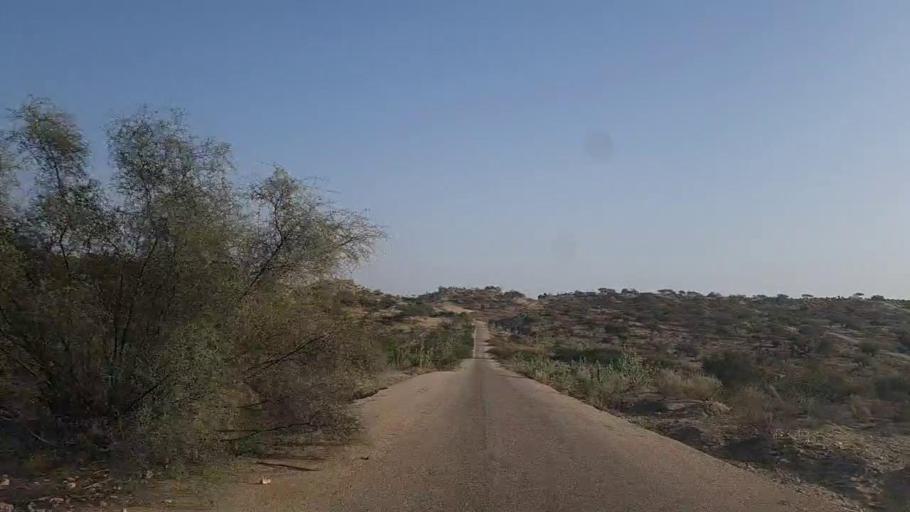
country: PK
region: Sindh
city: Diplo
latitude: 24.6038
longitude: 69.3799
